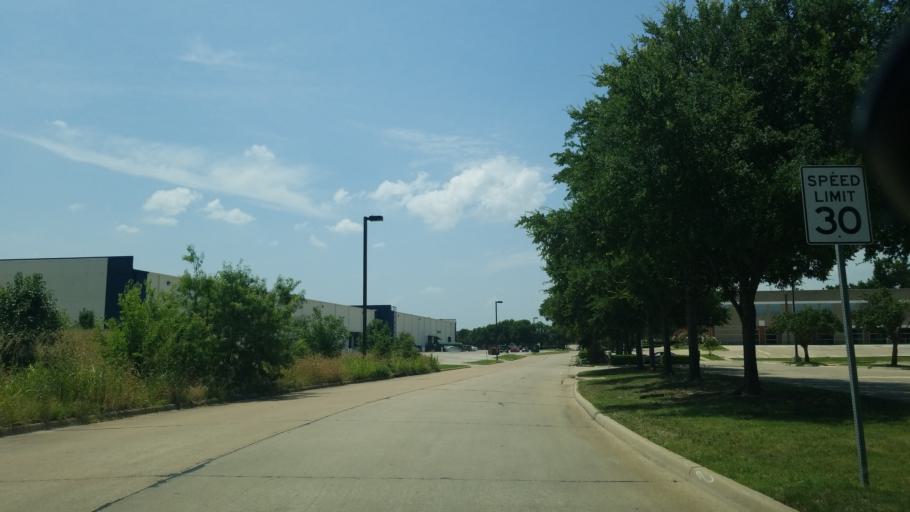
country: US
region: Texas
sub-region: Dallas County
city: Coppell
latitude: 32.9192
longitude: -96.9952
